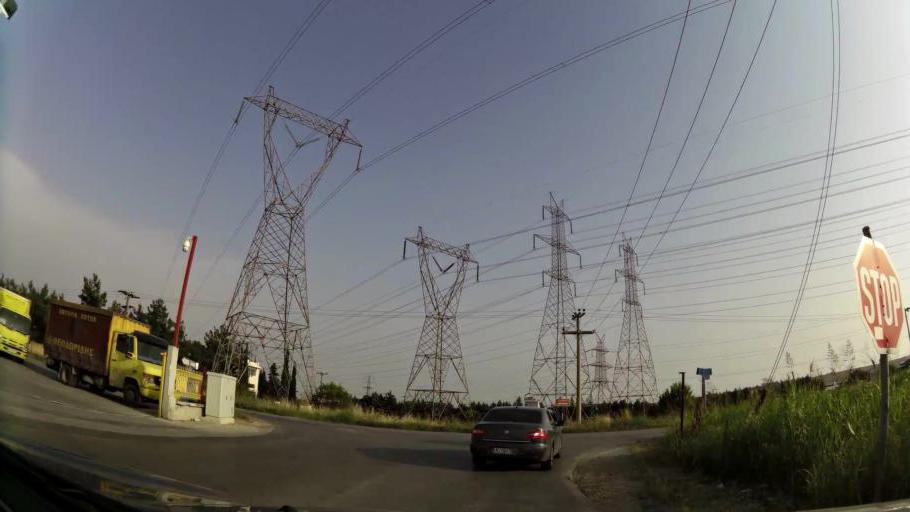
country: GR
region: Central Macedonia
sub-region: Nomos Thessalonikis
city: Oraiokastro
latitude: 40.7026
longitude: 22.9126
